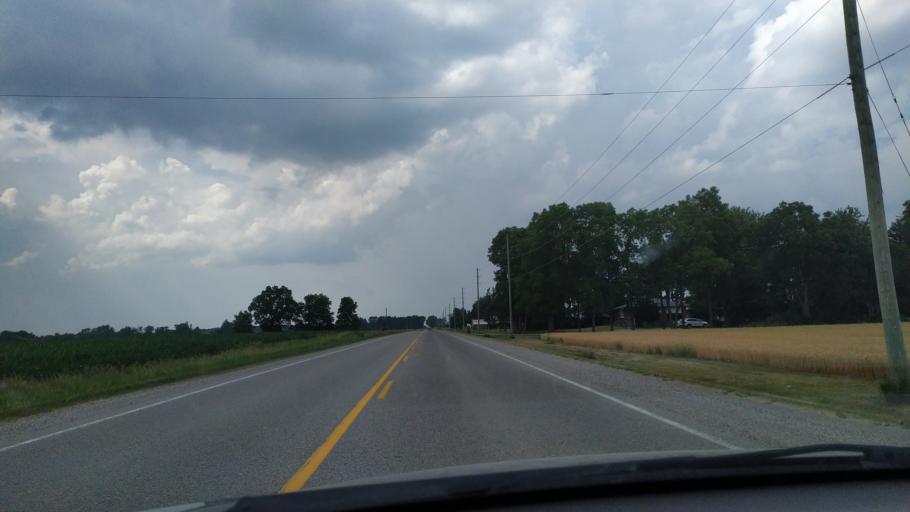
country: CA
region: Ontario
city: London
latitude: 43.1441
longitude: -81.1785
